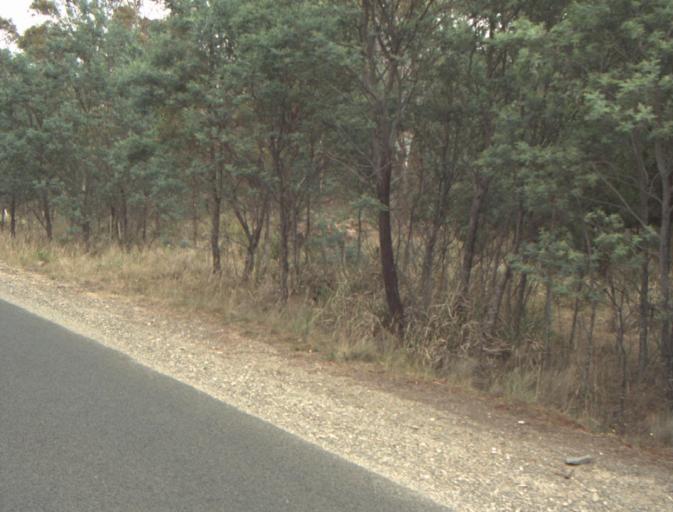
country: AU
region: Tasmania
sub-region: Northern Midlands
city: Evandale
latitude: -41.5081
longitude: 147.3518
